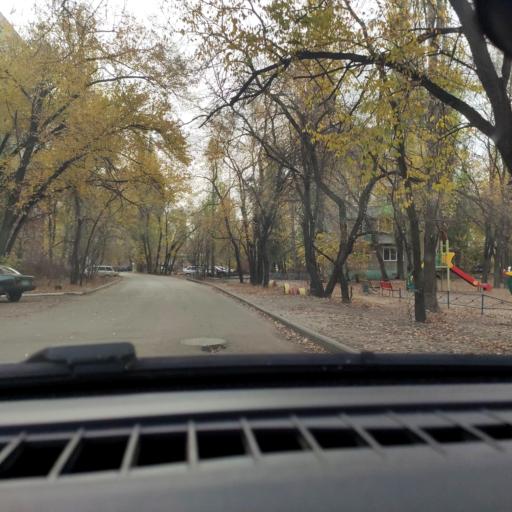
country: RU
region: Voronezj
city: Voronezh
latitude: 51.7097
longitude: 39.2719
